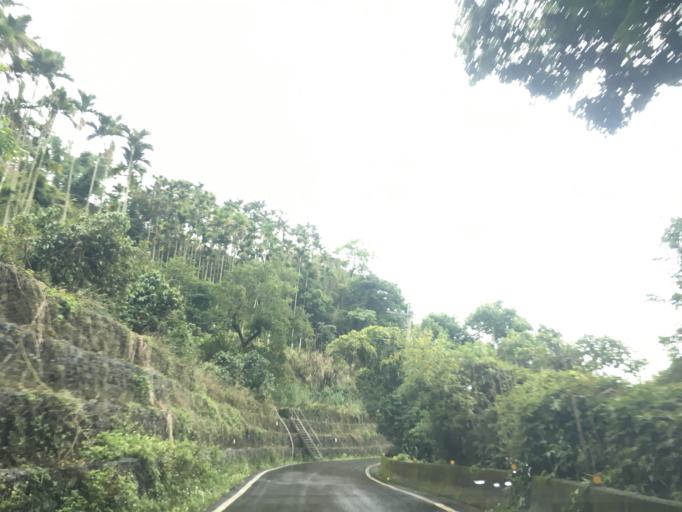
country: TW
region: Taiwan
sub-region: Yunlin
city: Douliu
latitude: 23.5602
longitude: 120.6555
